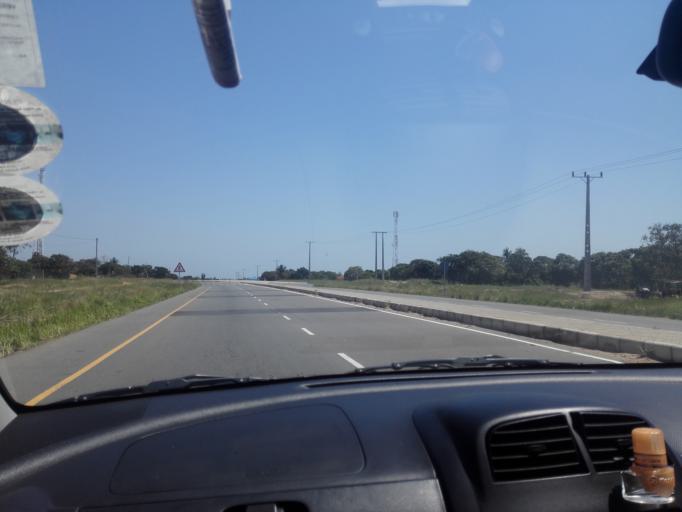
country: MZ
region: Maputo City
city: Maputo
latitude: -25.8133
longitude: 32.6728
